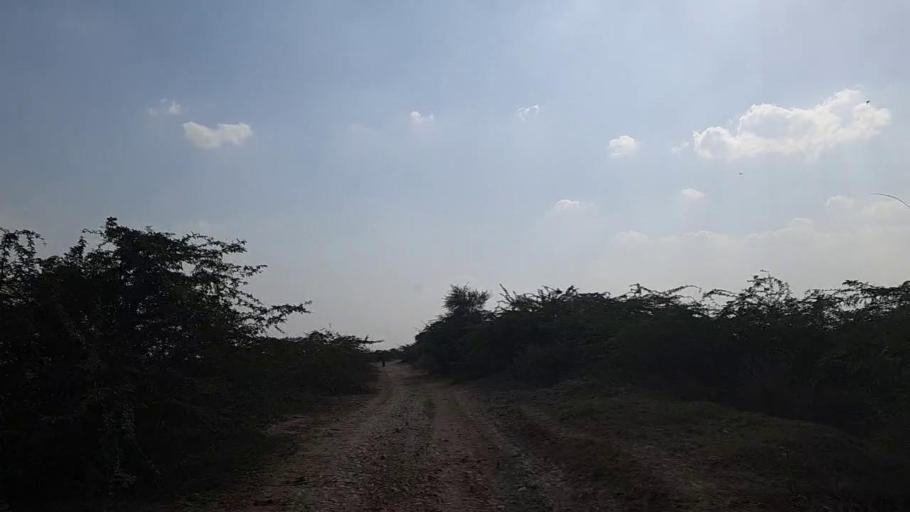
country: PK
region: Sindh
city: Jati
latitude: 24.4854
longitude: 68.3428
